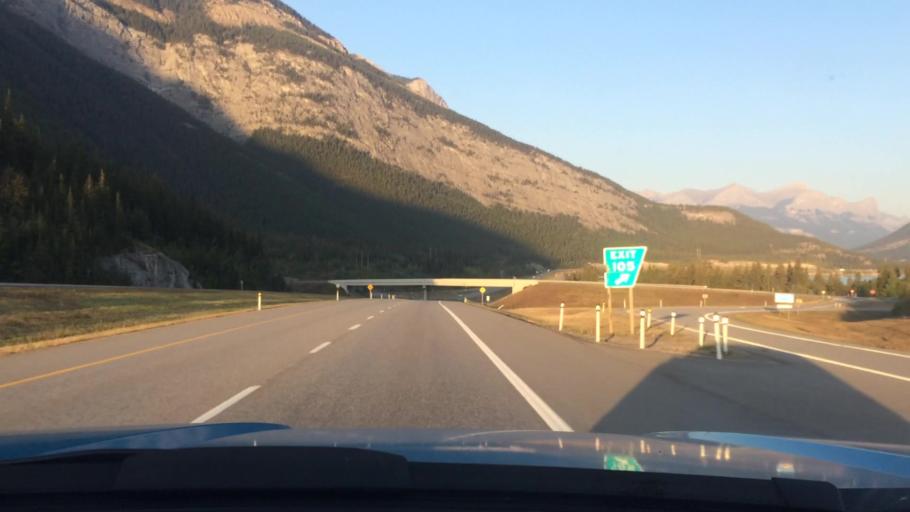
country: CA
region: Alberta
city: Canmore
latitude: 51.0507
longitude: -115.1594
